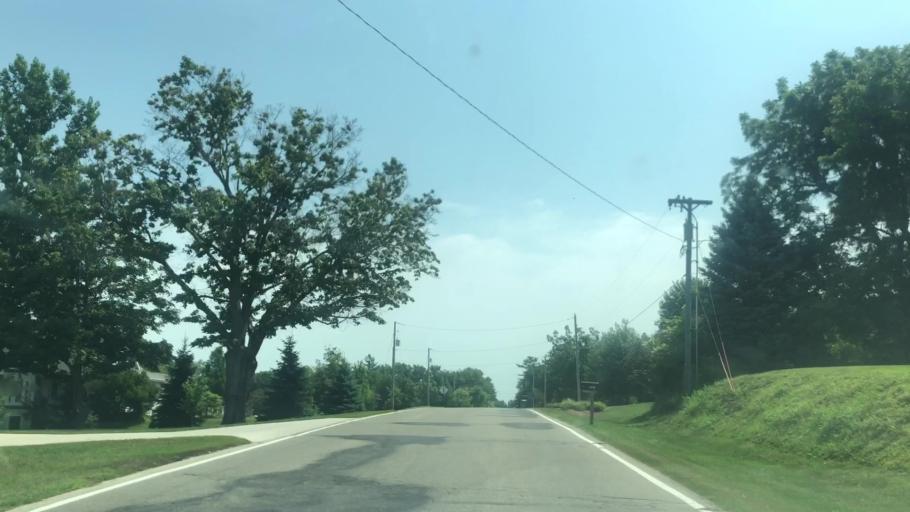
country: US
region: Iowa
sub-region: Marshall County
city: Marshalltown
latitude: 42.0287
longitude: -92.9454
